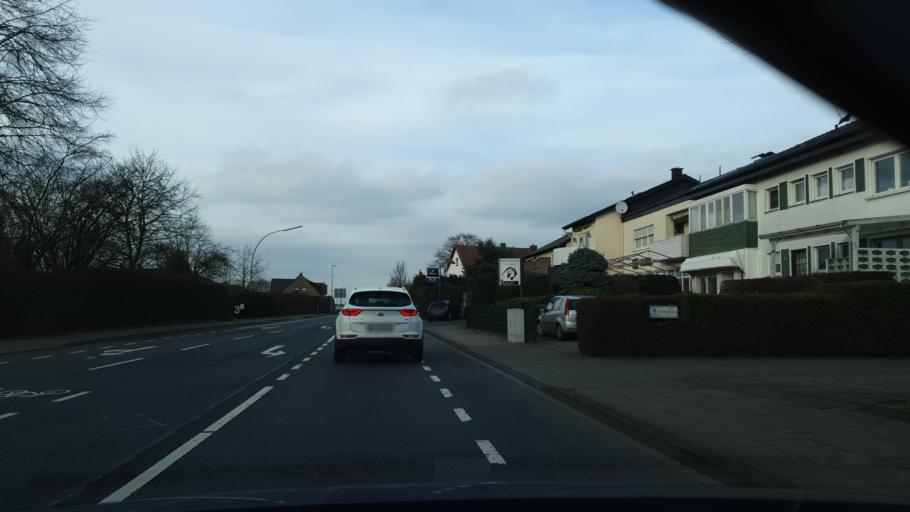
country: DE
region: North Rhine-Westphalia
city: Spenge
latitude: 52.0980
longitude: 8.5134
